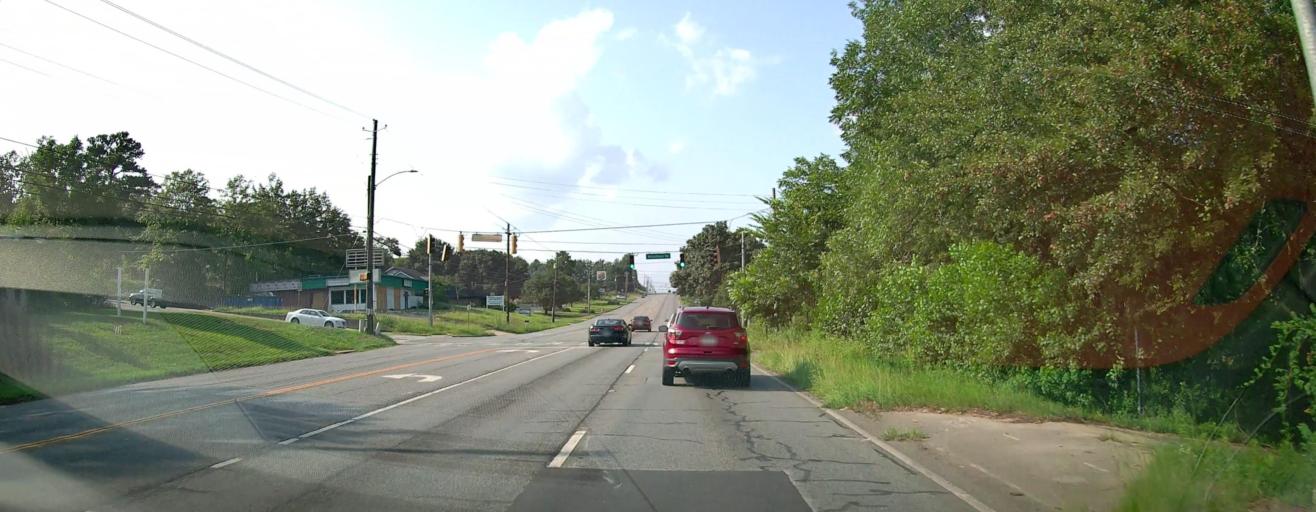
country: US
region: Georgia
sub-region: Bibb County
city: Macon
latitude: 32.8056
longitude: -83.6630
